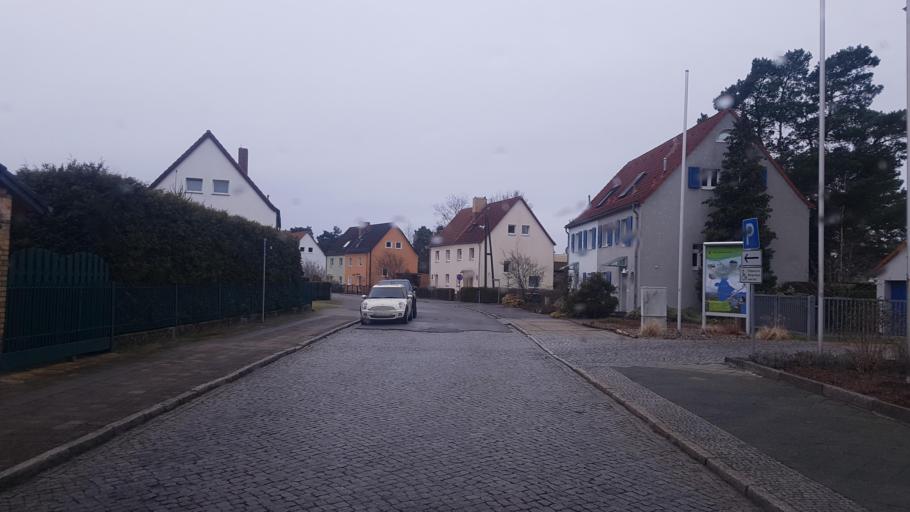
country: DE
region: Brandenburg
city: Schwarzheide
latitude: 51.4772
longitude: 13.8559
